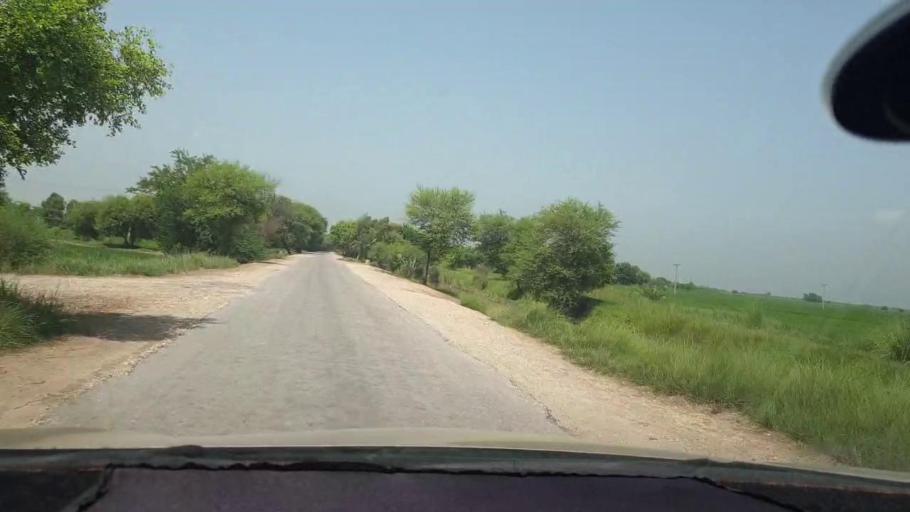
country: PK
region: Sindh
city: Kambar
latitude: 27.6525
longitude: 67.9645
